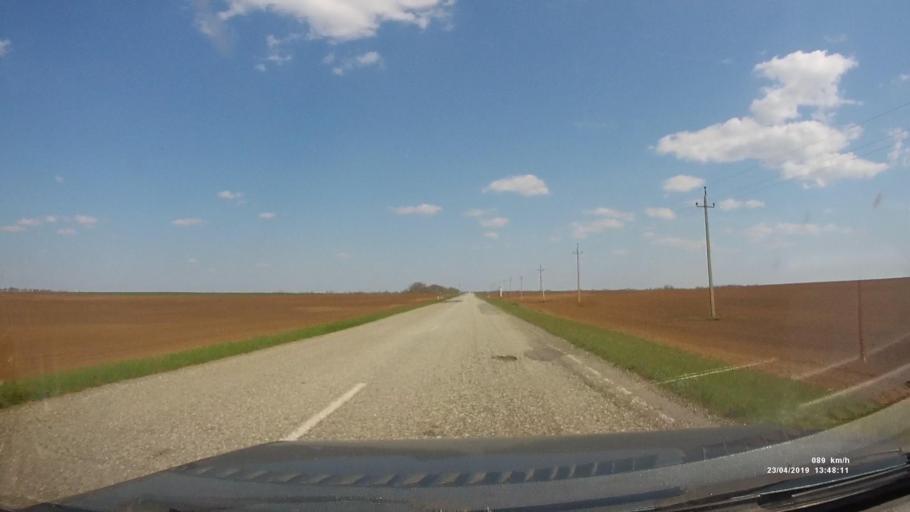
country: RU
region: Kalmykiya
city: Yashalta
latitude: 46.5991
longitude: 42.8687
